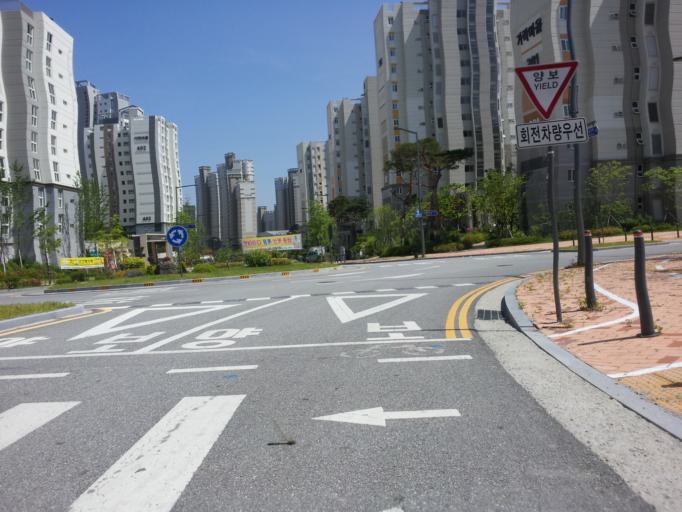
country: KR
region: Chungcheongnam-do
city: Gongju
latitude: 36.5077
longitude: 127.2354
